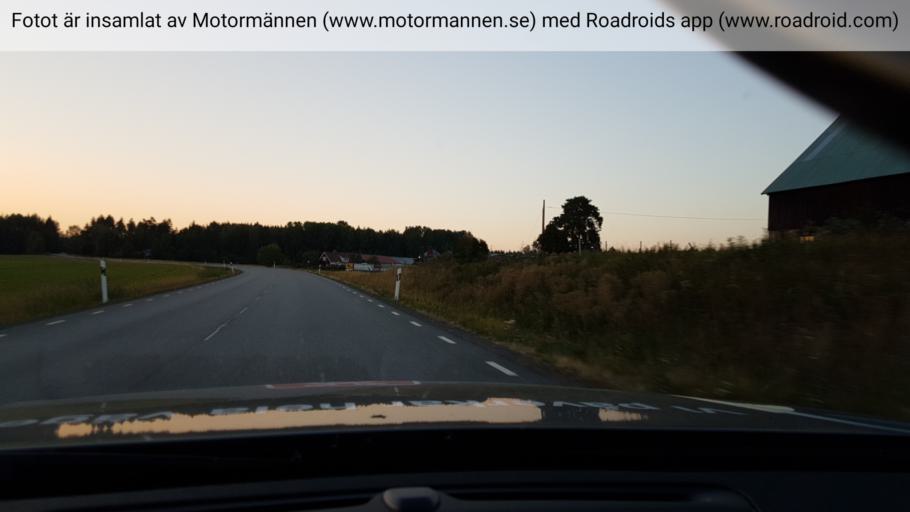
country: SE
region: Uppsala
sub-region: Heby Kommun
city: OEstervala
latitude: 60.1258
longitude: 17.2215
